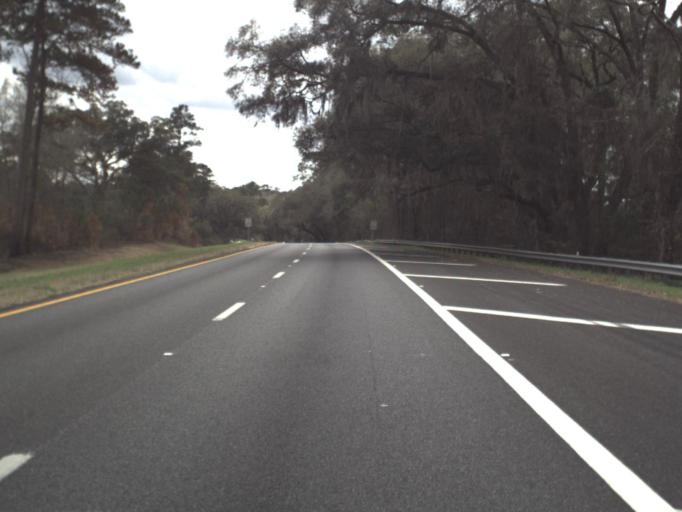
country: US
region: Georgia
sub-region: Grady County
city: Cairo
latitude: 30.6647
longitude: -84.1667
